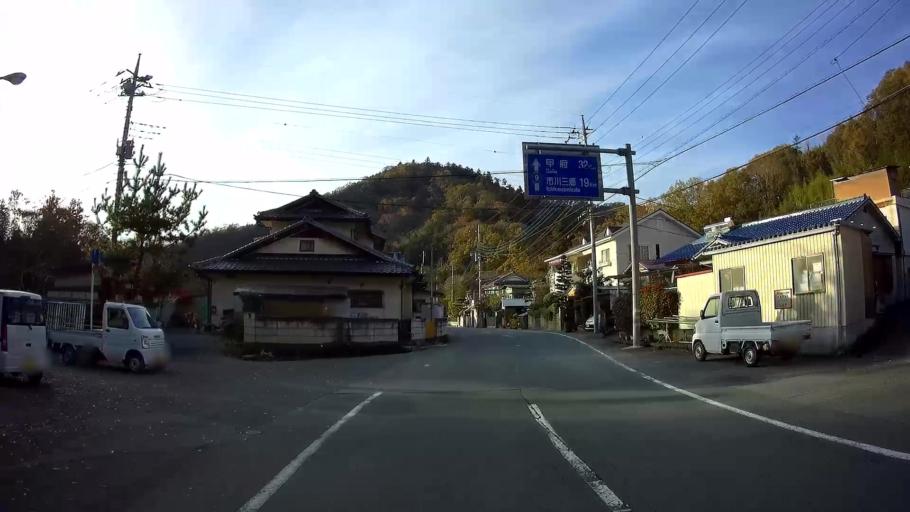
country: JP
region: Yamanashi
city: Ryuo
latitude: 35.4636
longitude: 138.4907
